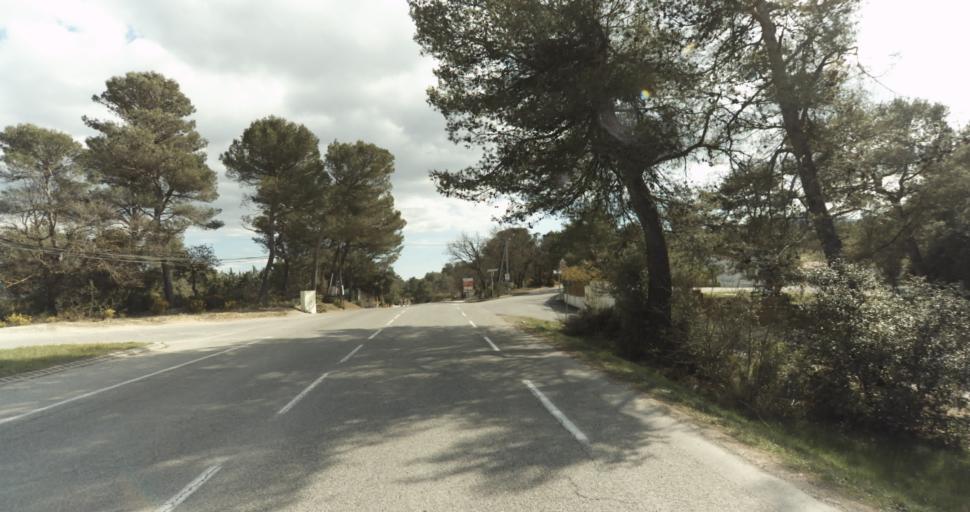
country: FR
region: Provence-Alpes-Cote d'Azur
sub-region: Departement des Bouches-du-Rhone
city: Greasque
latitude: 43.4407
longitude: 5.5291
